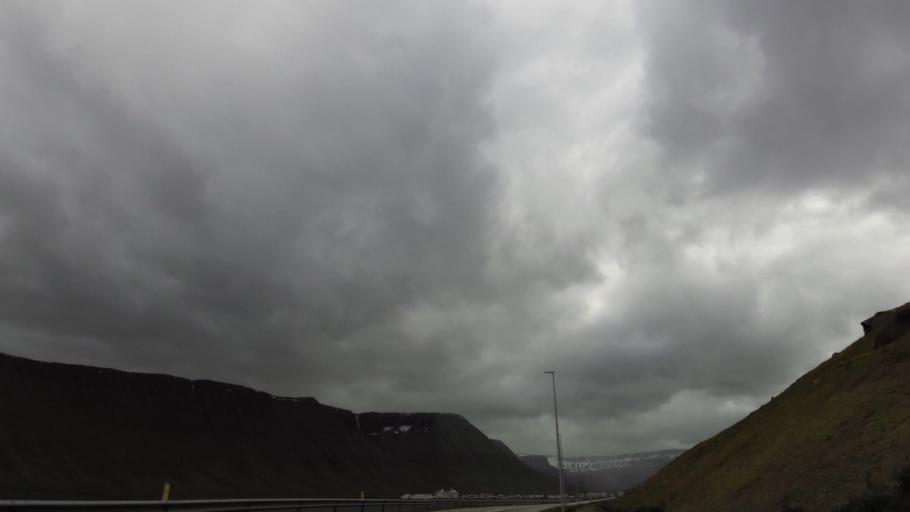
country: IS
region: Westfjords
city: Isafjoerdur
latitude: 66.0923
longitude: -23.1137
